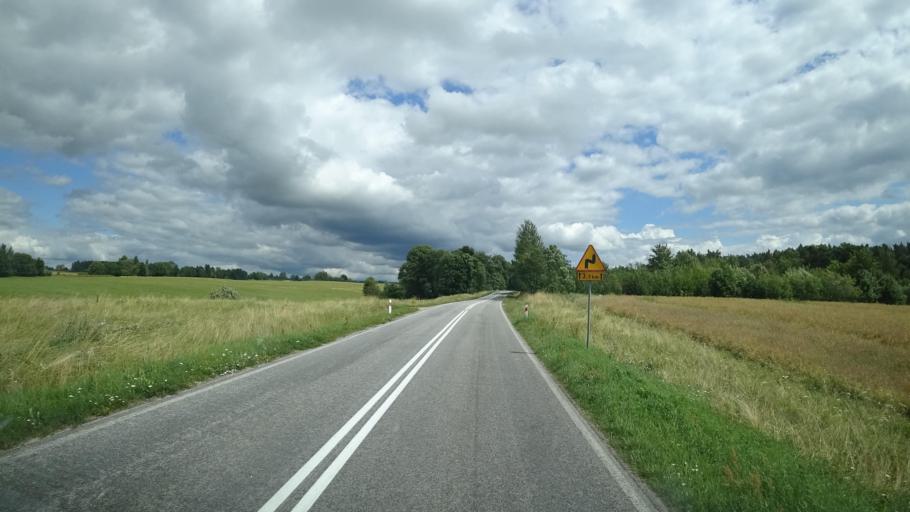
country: PL
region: Warmian-Masurian Voivodeship
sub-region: Powiat goldapski
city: Banie Mazurskie
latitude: 54.2123
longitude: 22.1722
